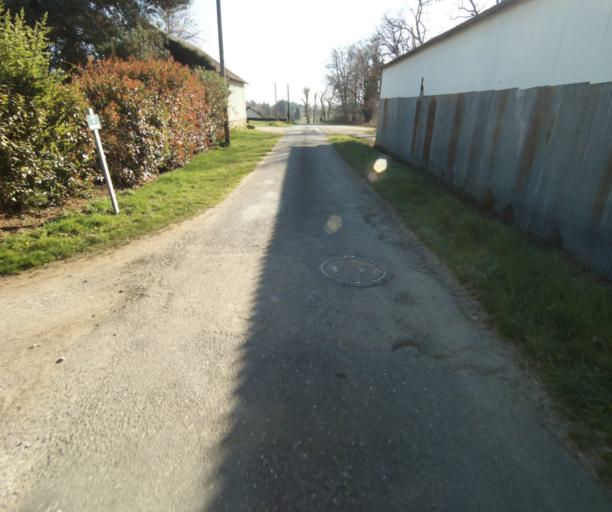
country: FR
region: Limousin
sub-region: Departement de la Correze
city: Chamboulive
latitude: 45.4759
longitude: 1.7254
